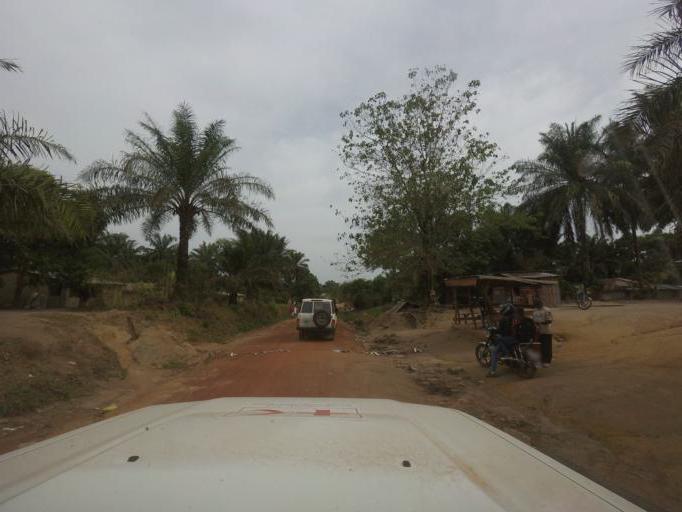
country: SL
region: Eastern Province
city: Buedu
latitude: 8.3810
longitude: -10.2043
